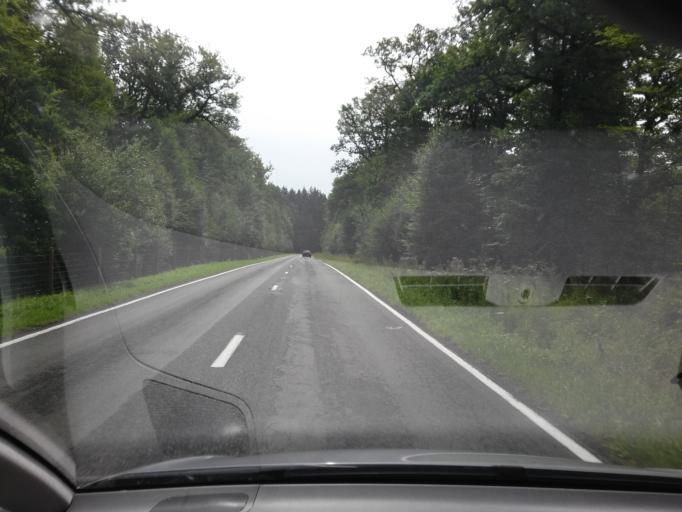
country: BE
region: Wallonia
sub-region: Province du Luxembourg
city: Chiny
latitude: 49.7719
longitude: 5.3577
